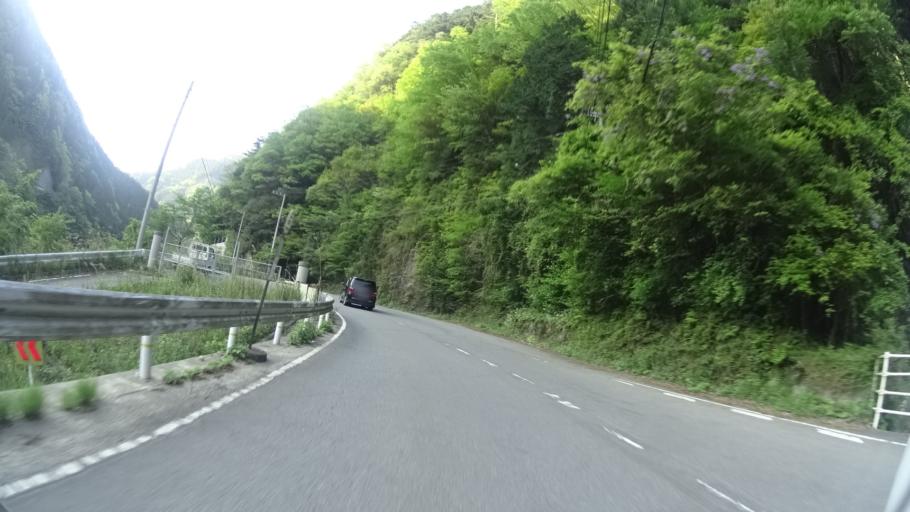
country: JP
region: Tokushima
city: Ikedacho
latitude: 33.8742
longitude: 133.8700
